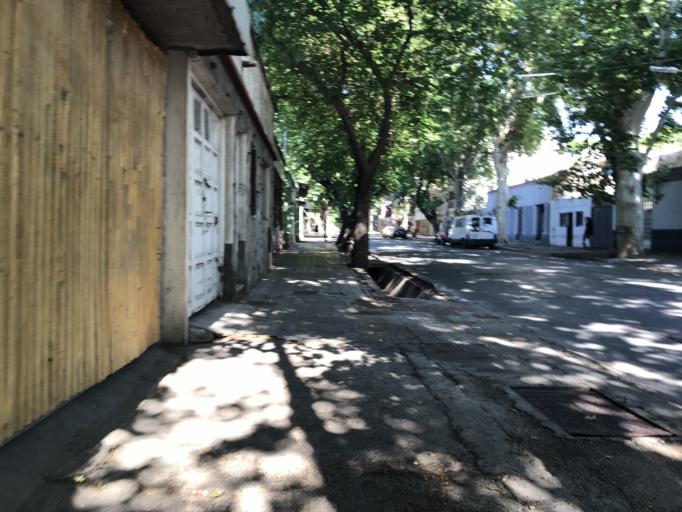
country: AR
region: Mendoza
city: Mendoza
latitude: -32.8764
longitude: -68.8337
